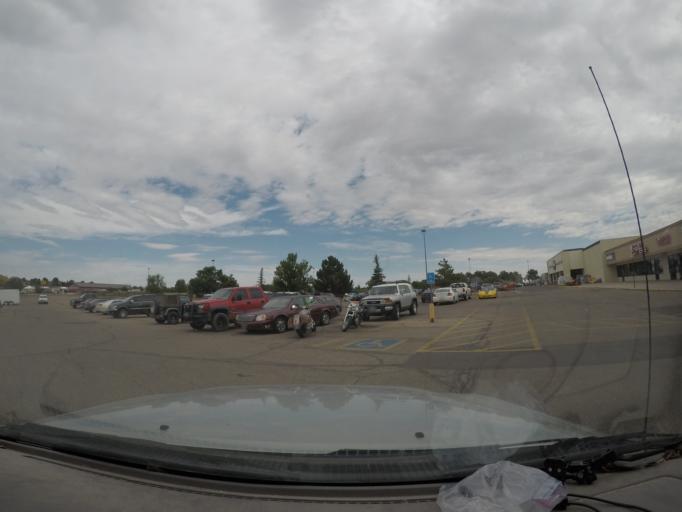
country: US
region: Wyoming
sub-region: Laramie County
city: Fox Farm-College
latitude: 41.1385
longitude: -104.7638
